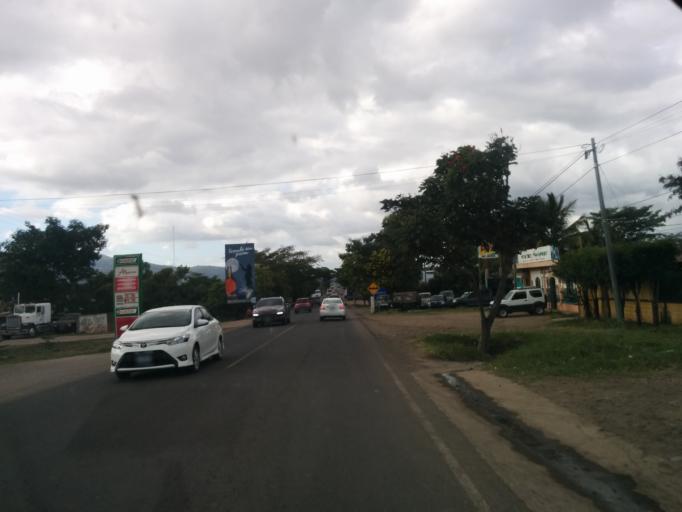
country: NI
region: Esteli
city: Esteli
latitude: 13.0641
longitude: -86.3468
